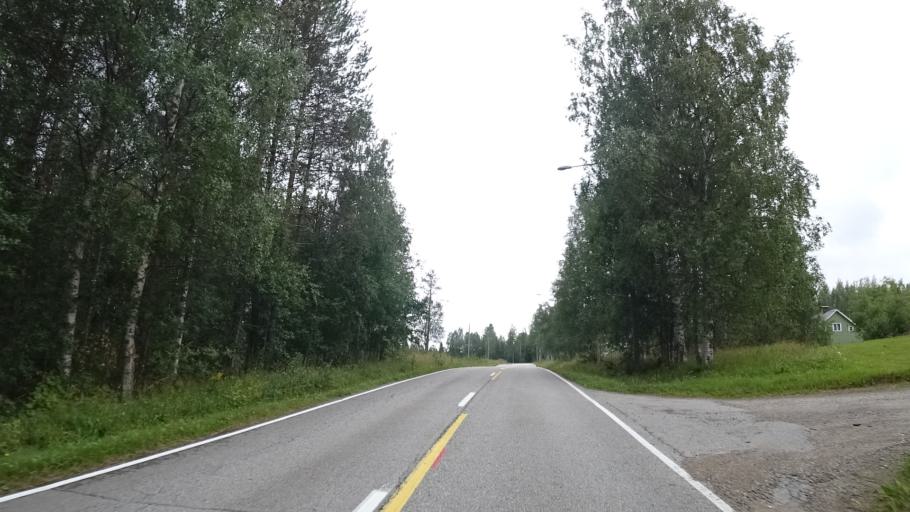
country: FI
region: North Karelia
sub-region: Joensuu
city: Ilomantsi
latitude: 62.9377
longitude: 31.2846
